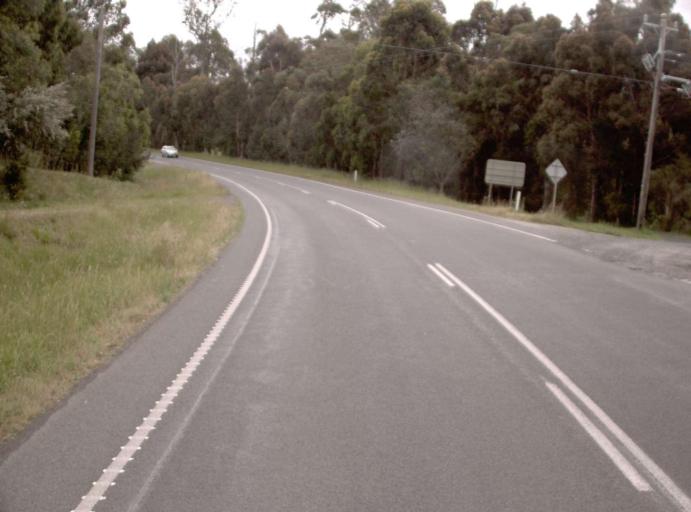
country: AU
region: Victoria
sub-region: Baw Baw
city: Warragul
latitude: -38.0463
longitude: 145.9564
